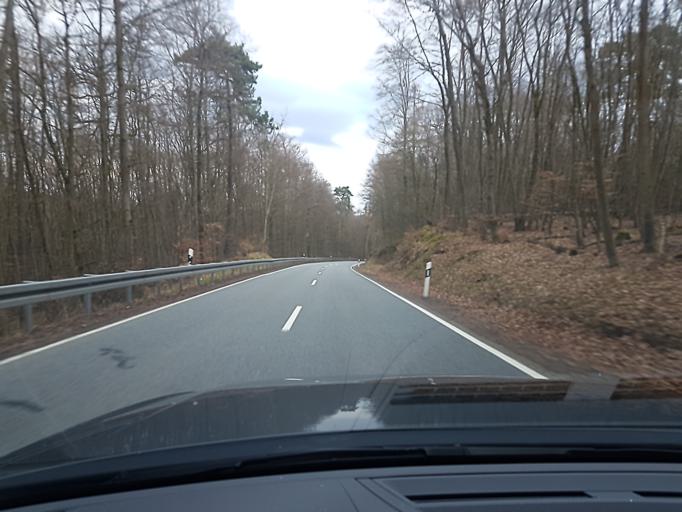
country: DE
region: Hesse
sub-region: Regierungsbezirk Giessen
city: Merkenbach
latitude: 50.6438
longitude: 8.2871
